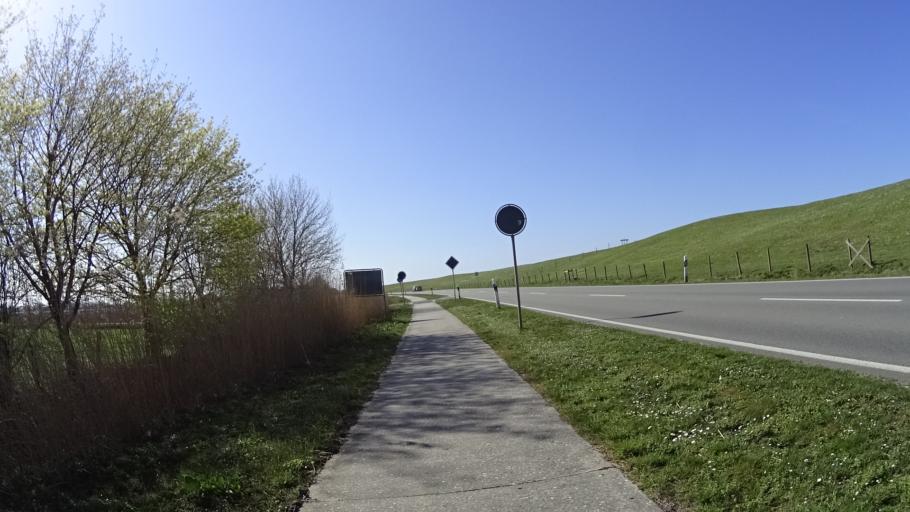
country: DE
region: Lower Saxony
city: Jemgum
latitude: 53.2603
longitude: 7.4062
